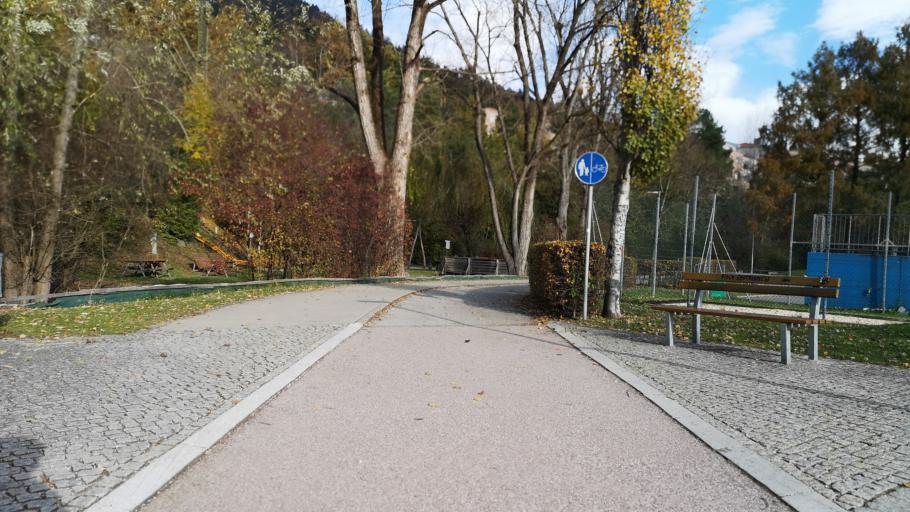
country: AT
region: Tyrol
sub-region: Politischer Bezirk Innsbruck Land
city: Vols
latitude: 47.2675
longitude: 11.3434
